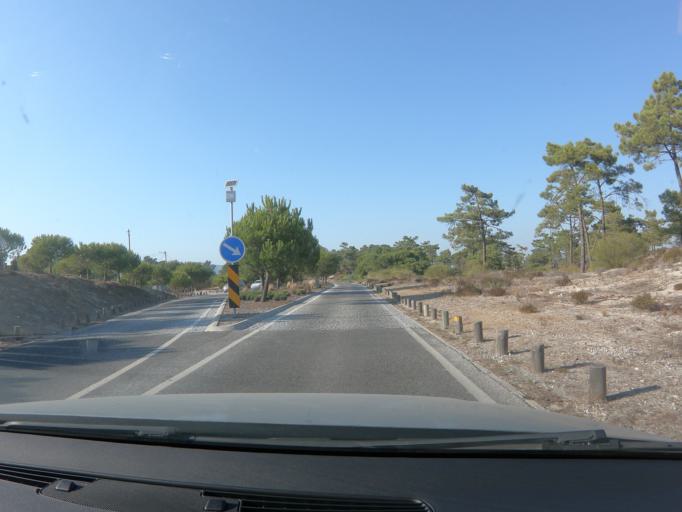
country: PT
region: Setubal
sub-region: Setubal
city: Setubal
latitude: 38.4727
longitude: -8.8848
